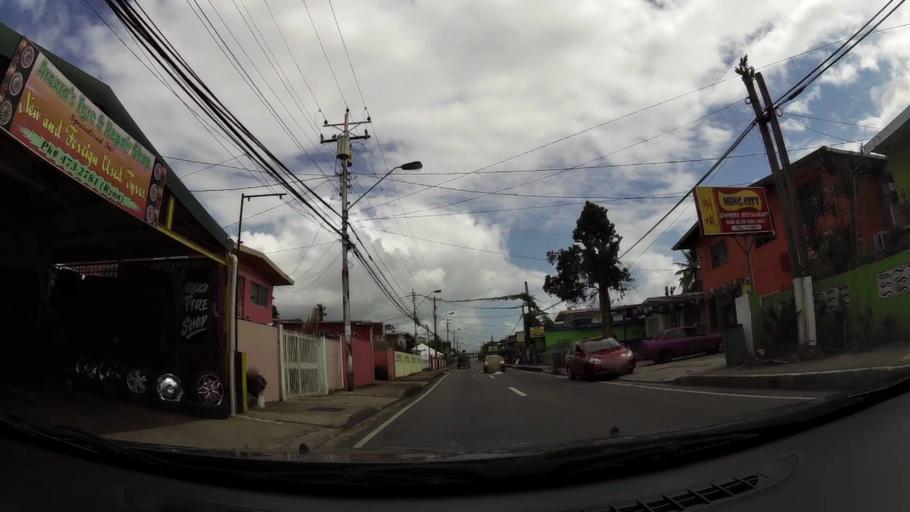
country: TT
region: Tunapuna/Piarco
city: Arouca
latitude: 10.6341
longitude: -61.3307
